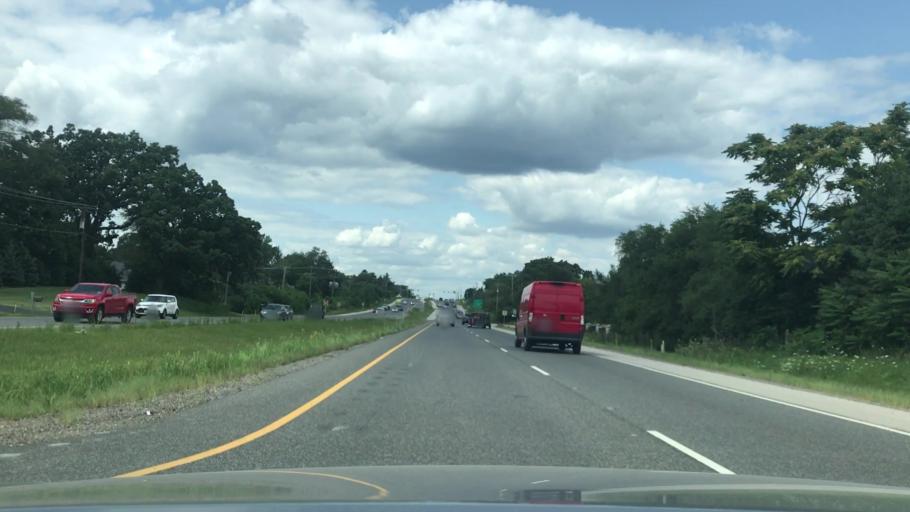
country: US
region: Illinois
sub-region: DuPage County
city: Burr Ridge
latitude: 41.7285
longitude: -87.9438
